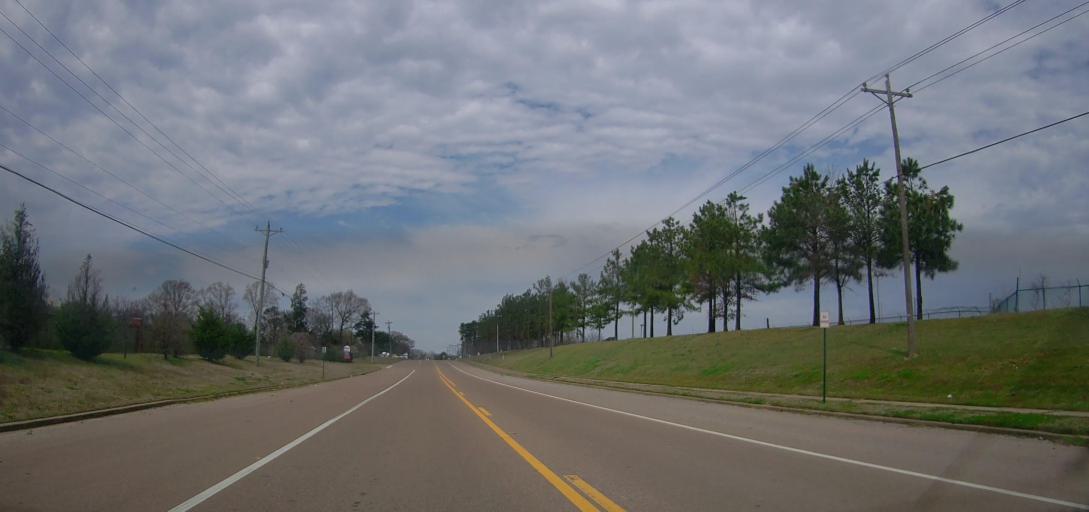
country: US
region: Mississippi
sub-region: De Soto County
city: Olive Branch
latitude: 34.9783
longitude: -89.8509
